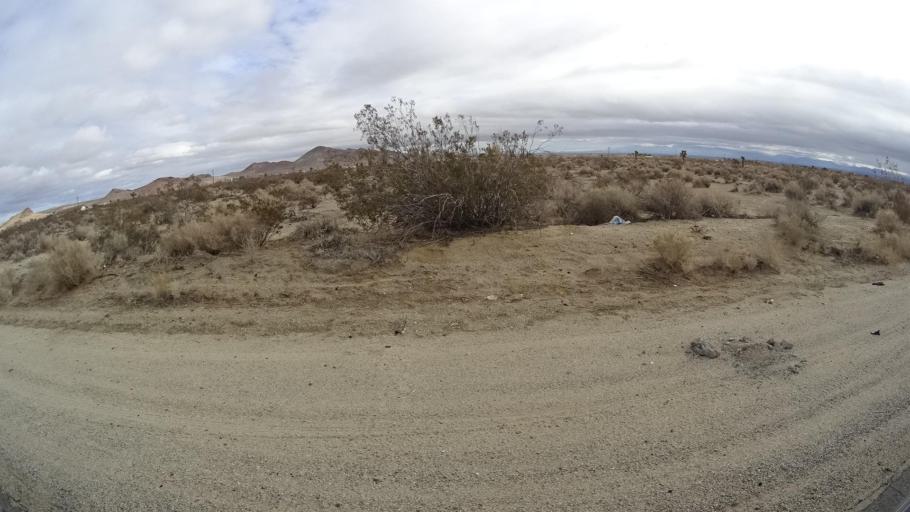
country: US
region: California
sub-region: Kern County
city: Rosamond
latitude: 34.8880
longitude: -118.2233
